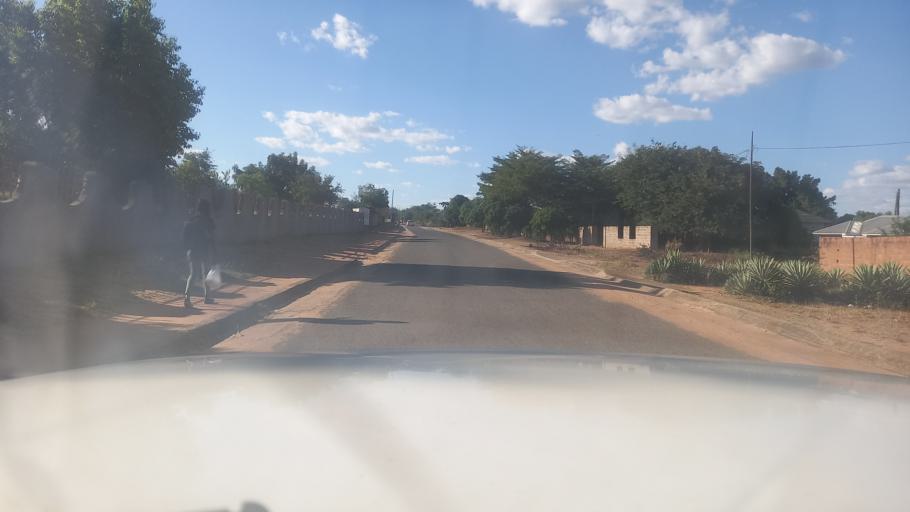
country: ZM
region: Southern
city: Livingstone
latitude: -17.8318
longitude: 25.8660
